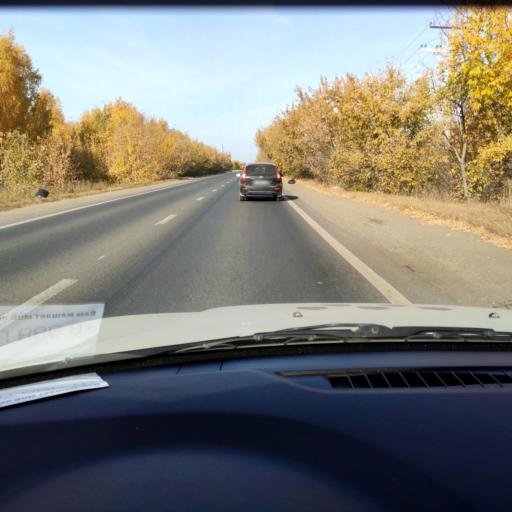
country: RU
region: Samara
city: Tol'yatti
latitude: 53.5571
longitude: 49.3630
